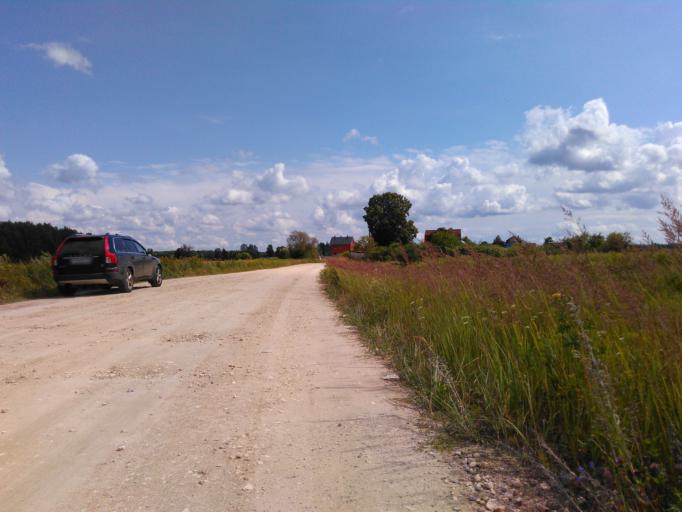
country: RU
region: Vladimir
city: Krasnyy Oktyabr'
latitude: 56.0018
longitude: 38.8469
